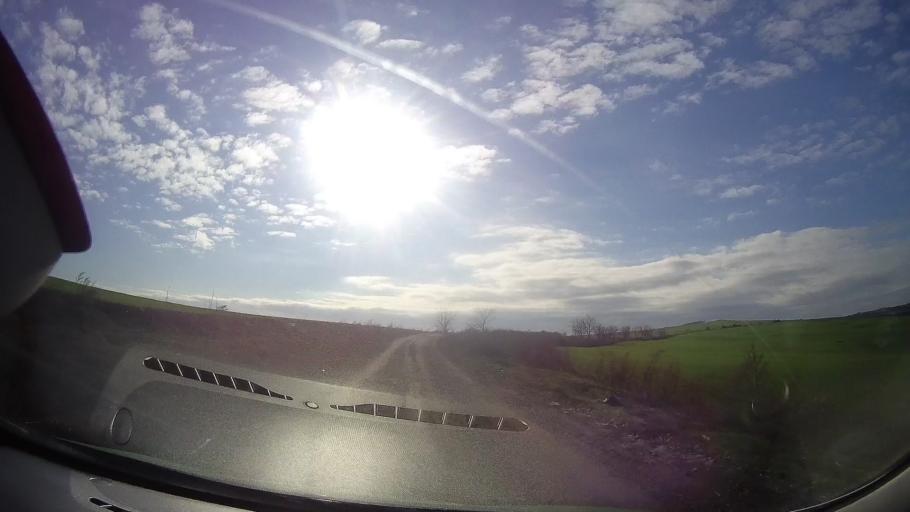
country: RO
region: Mures
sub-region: Comuna Saulia
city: Saulia
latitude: 46.6059
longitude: 24.2432
